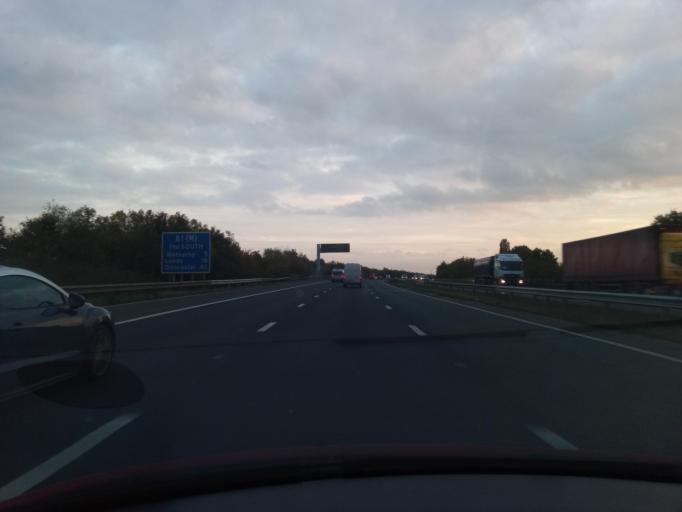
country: GB
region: England
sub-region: City and Borough of Leeds
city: Wetherby
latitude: 54.0030
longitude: -1.3707
